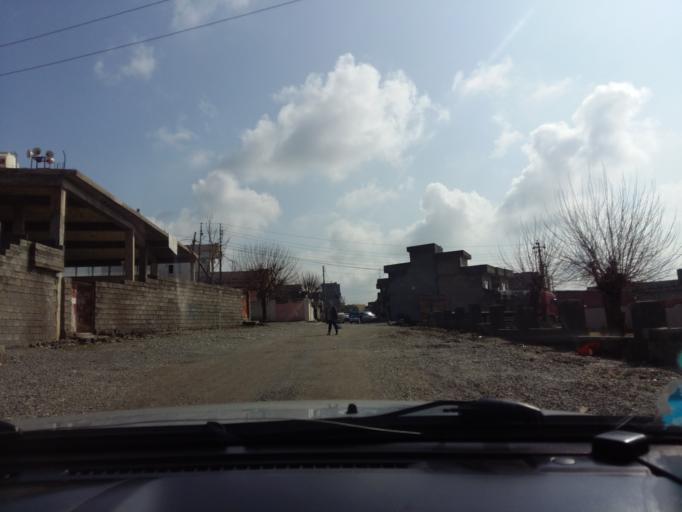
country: IQ
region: As Sulaymaniyah
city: Qeladize
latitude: 36.1921
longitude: 45.1230
